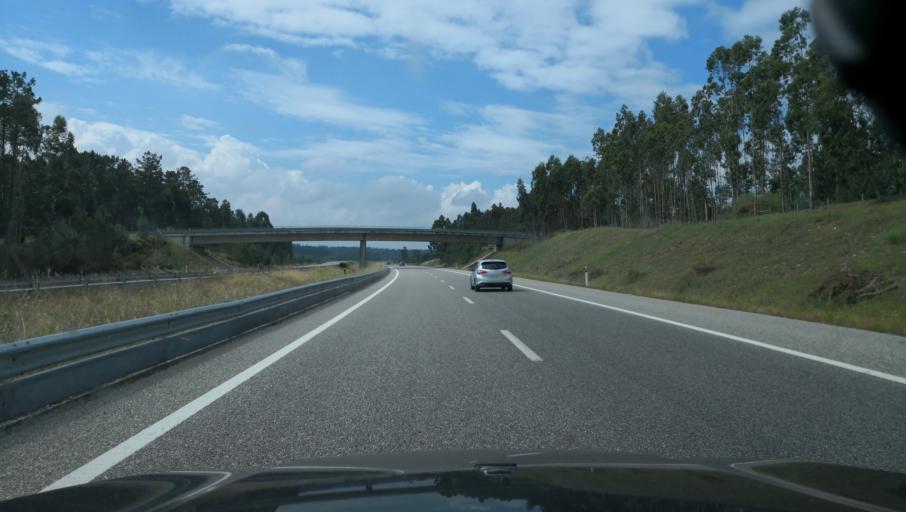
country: PT
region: Leiria
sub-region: Leiria
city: Amor
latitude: 39.7788
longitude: -8.8689
